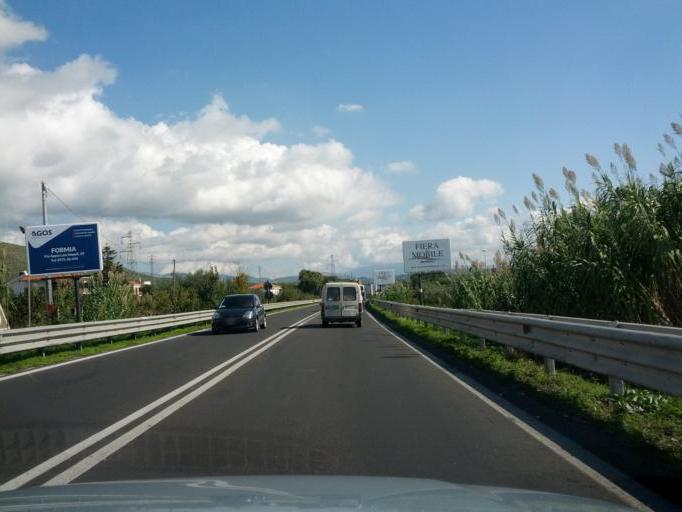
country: IT
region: Latium
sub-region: Provincia di Latina
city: Formia
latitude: 41.2673
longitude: 13.6639
